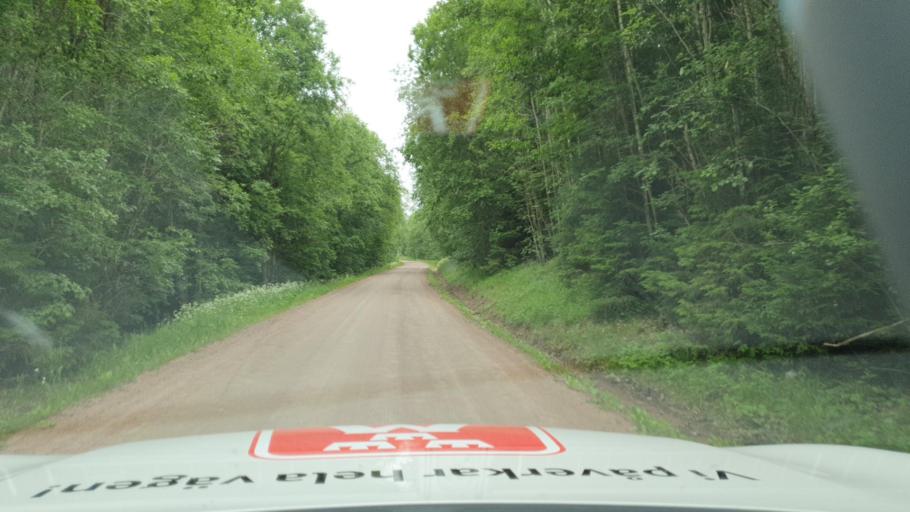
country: SE
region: Vaermland
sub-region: Filipstads Kommun
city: Filipstad
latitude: 59.5429
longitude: 13.9713
